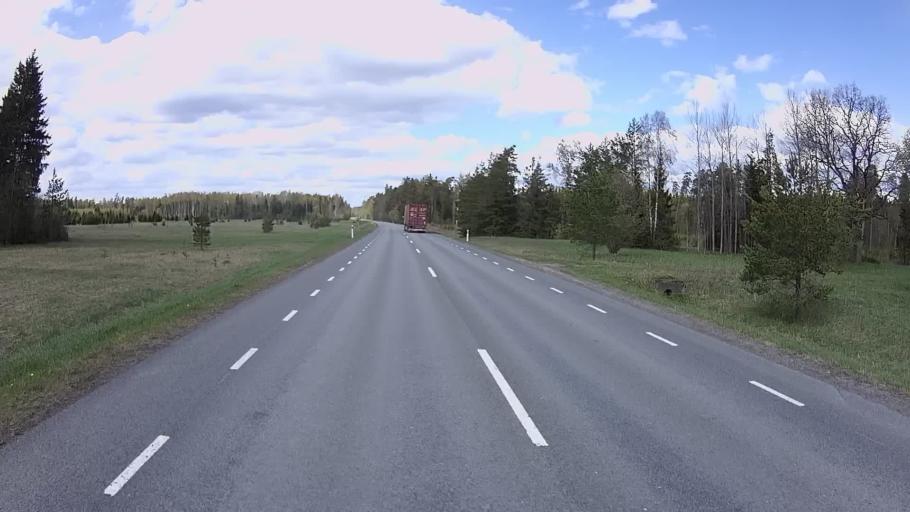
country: EE
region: Jaervamaa
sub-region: Jaerva-Jaani vald
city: Jarva-Jaani
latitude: 59.0906
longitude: 25.8315
